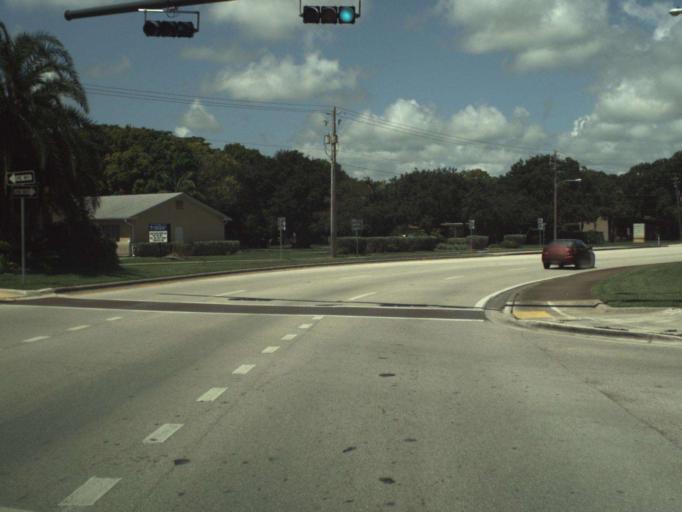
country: US
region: Florida
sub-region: Indian River County
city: Vero Beach
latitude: 27.6385
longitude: -80.4057
